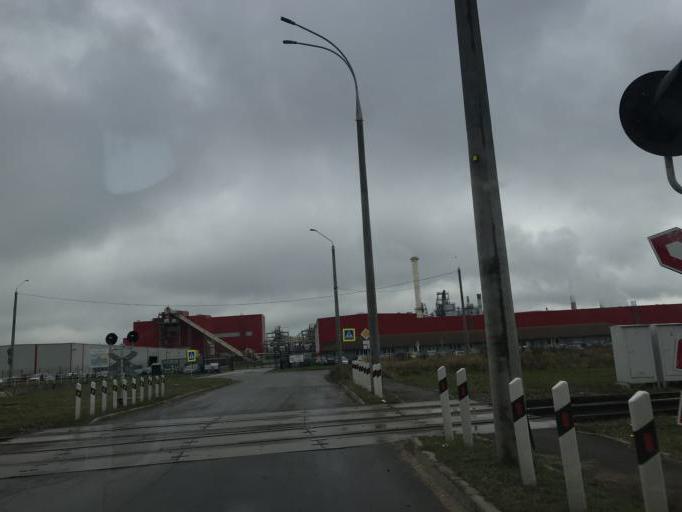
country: BY
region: Mogilev
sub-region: Mahilyowski Rayon
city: Veyno
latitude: 53.8240
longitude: 30.3524
